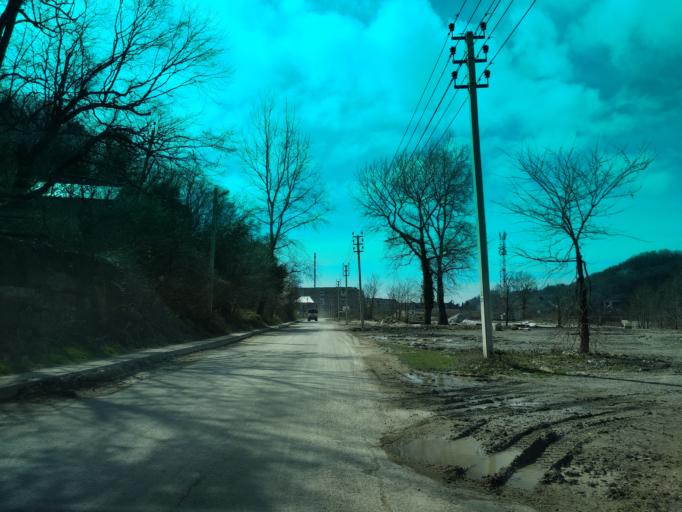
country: RU
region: Krasnodarskiy
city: Shepsi
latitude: 44.0466
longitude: 39.1571
